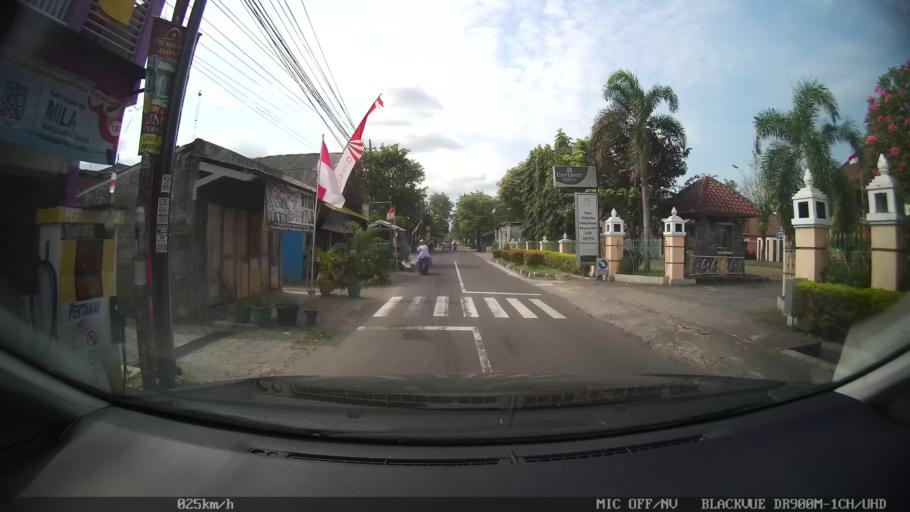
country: ID
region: Daerah Istimewa Yogyakarta
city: Depok
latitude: -7.7818
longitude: 110.4344
